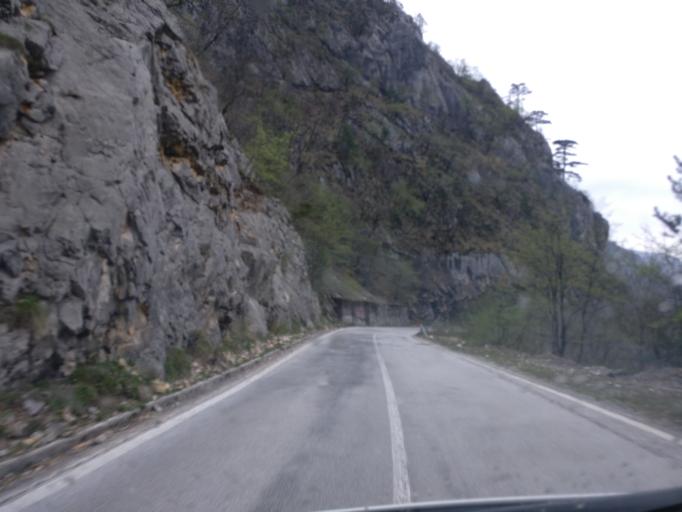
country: ME
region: Opstina Pluzine
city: Pluzine
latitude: 43.2394
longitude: 18.8419
